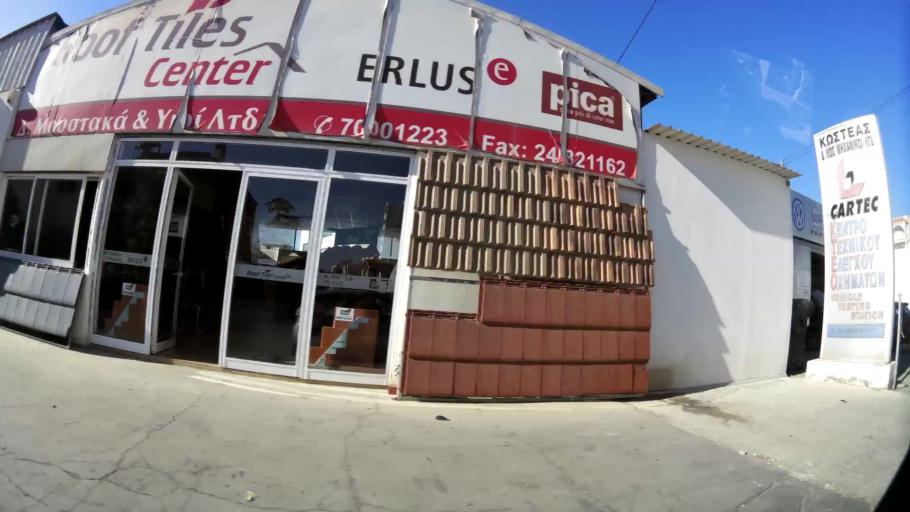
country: CY
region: Larnaka
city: Larnaca
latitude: 34.9269
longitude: 33.6165
